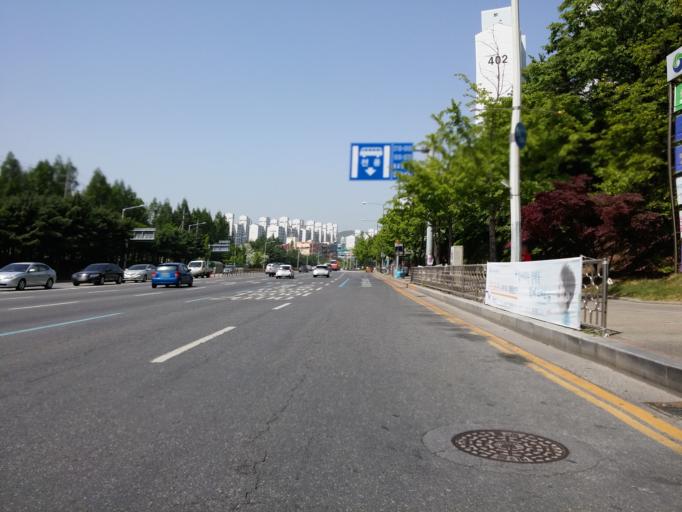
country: KR
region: Daejeon
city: Daejeon
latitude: 36.3026
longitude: 127.3403
